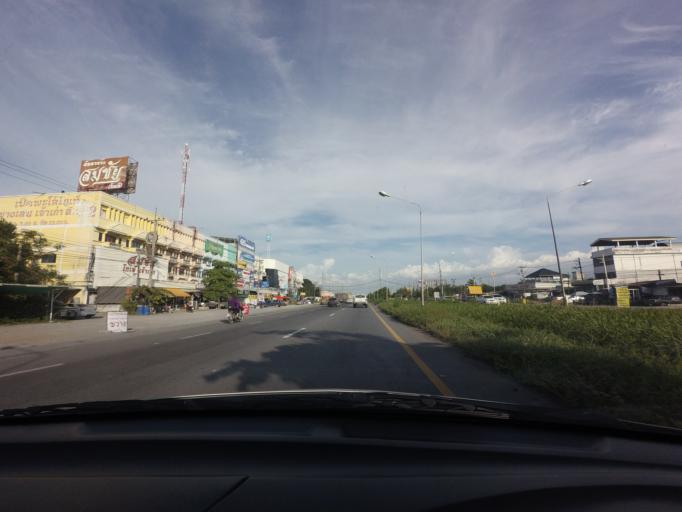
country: TH
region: Pathum Thani
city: Lat Lum Kaeo
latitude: 14.0316
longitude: 100.3509
